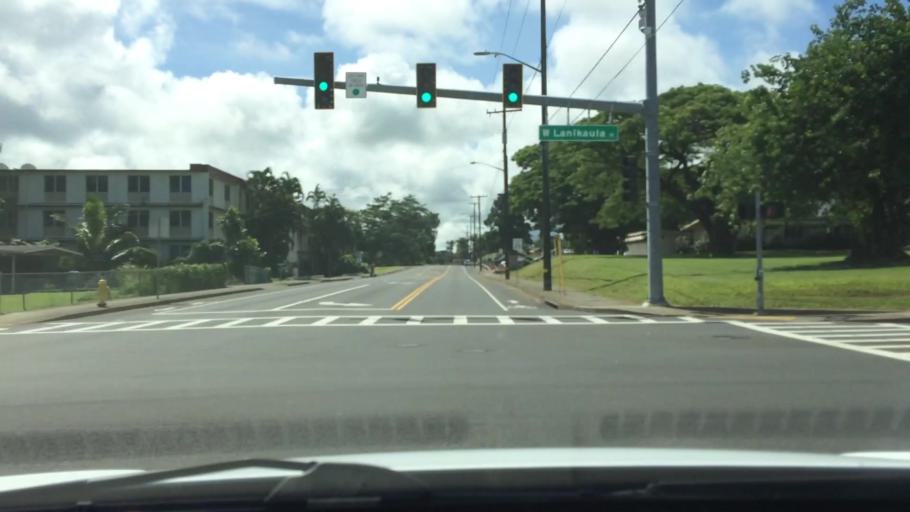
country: US
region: Hawaii
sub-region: Hawaii County
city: Hilo
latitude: 19.7046
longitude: -155.0796
